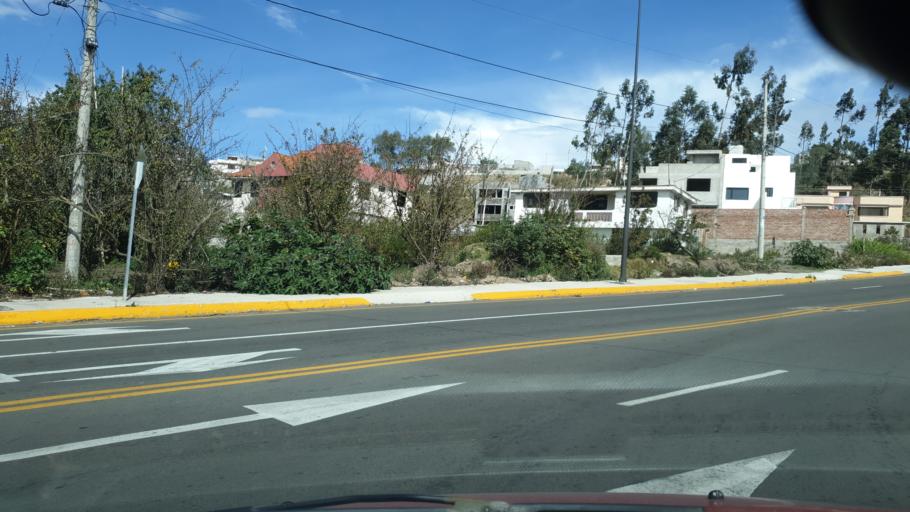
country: EC
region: Tungurahua
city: Ambato
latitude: -1.2904
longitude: -78.6302
